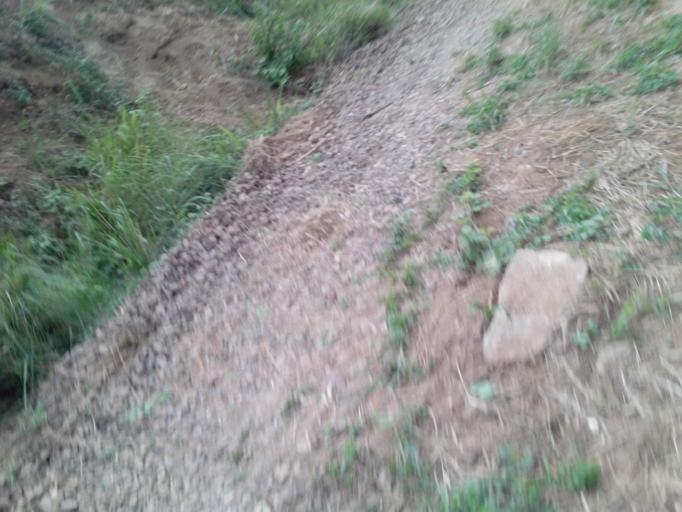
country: BR
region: Rio de Janeiro
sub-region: Miguel Pereira
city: Miguel Pereira
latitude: -22.5022
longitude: -43.5004
